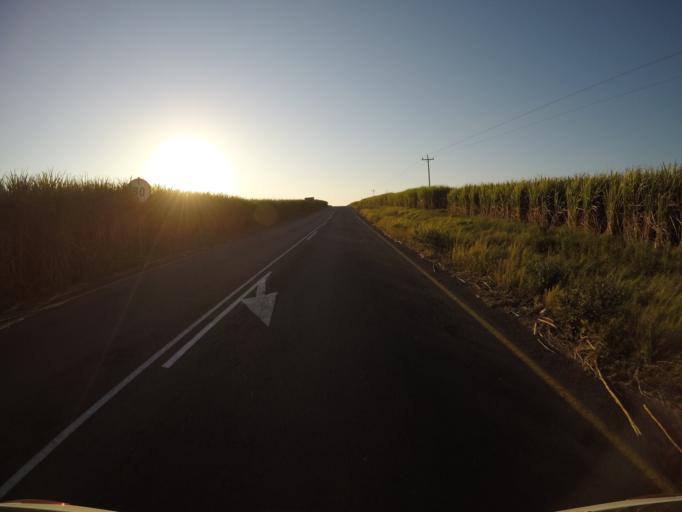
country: ZA
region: KwaZulu-Natal
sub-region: uThungulu District Municipality
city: eSikhawini
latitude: -28.9481
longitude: 31.7292
